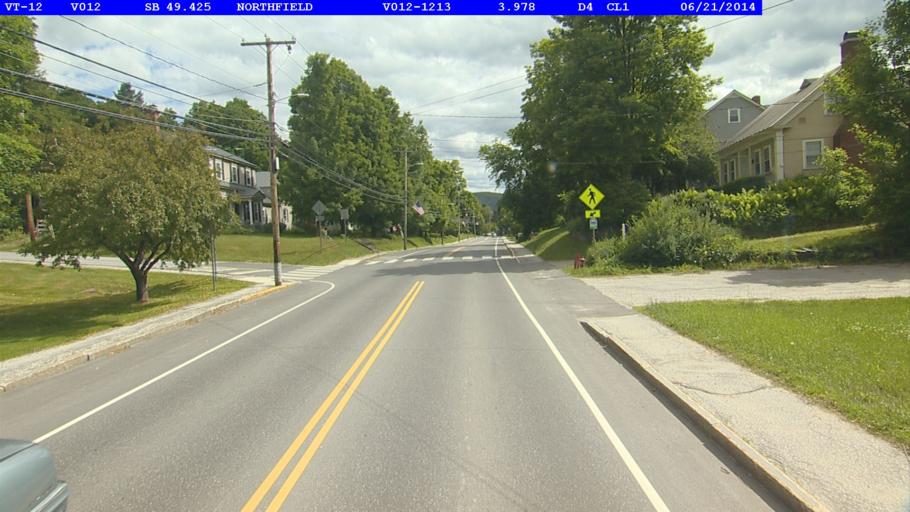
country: US
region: Vermont
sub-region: Washington County
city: Northfield
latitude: 44.1459
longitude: -72.6564
